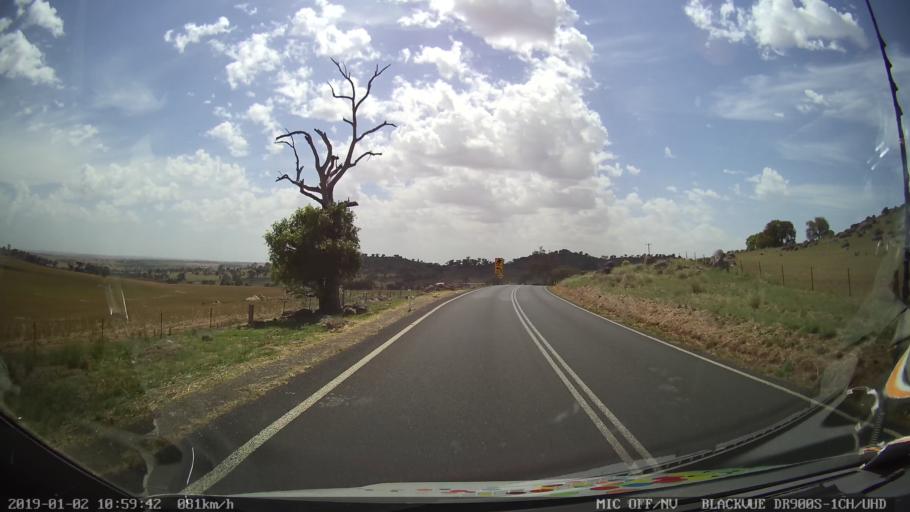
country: AU
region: New South Wales
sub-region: Cootamundra
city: Cootamundra
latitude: -34.6131
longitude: 148.3091
